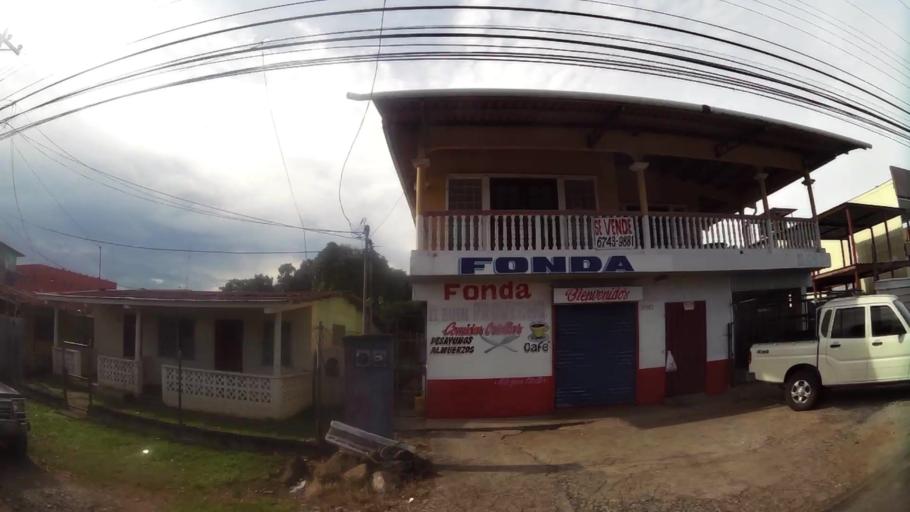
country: PA
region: Panama
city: La Chorrera
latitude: 8.8854
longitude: -79.7738
